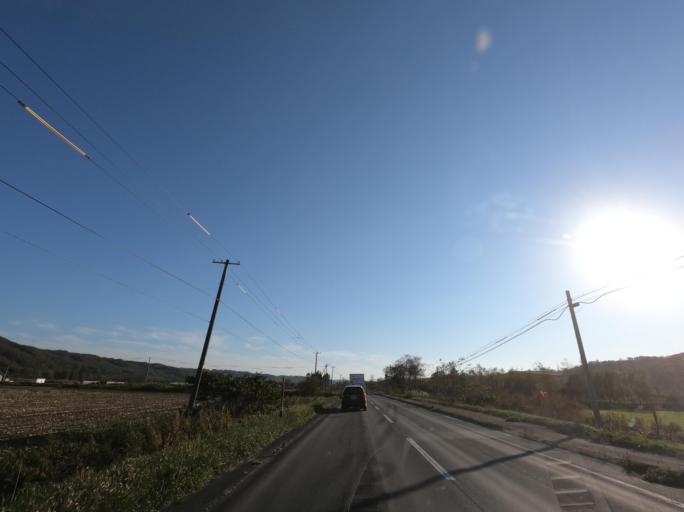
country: JP
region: Hokkaido
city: Kushiro
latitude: 43.1512
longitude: 144.1491
